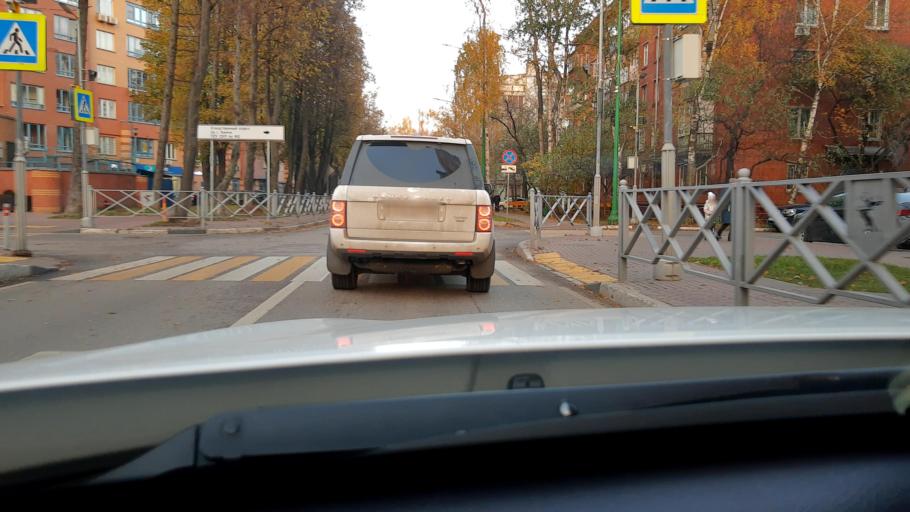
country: RU
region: Moscow
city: Khimki
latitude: 55.8858
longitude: 37.4473
